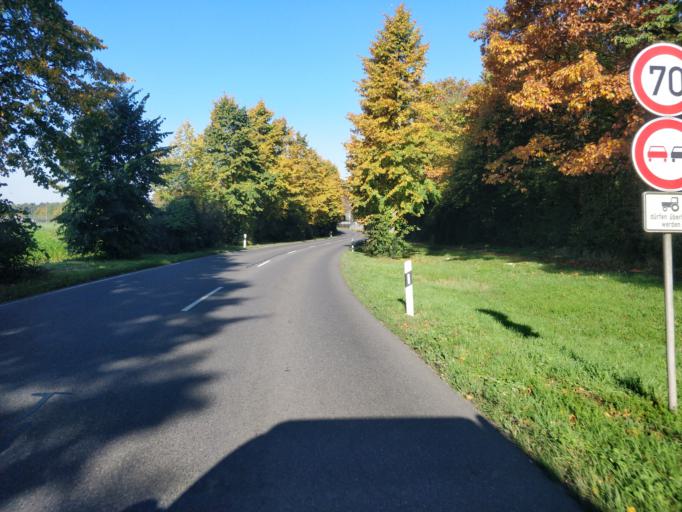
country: DE
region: North Rhine-Westphalia
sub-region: Regierungsbezirk Koln
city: Sinnersdorf
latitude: 51.0566
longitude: 6.8257
